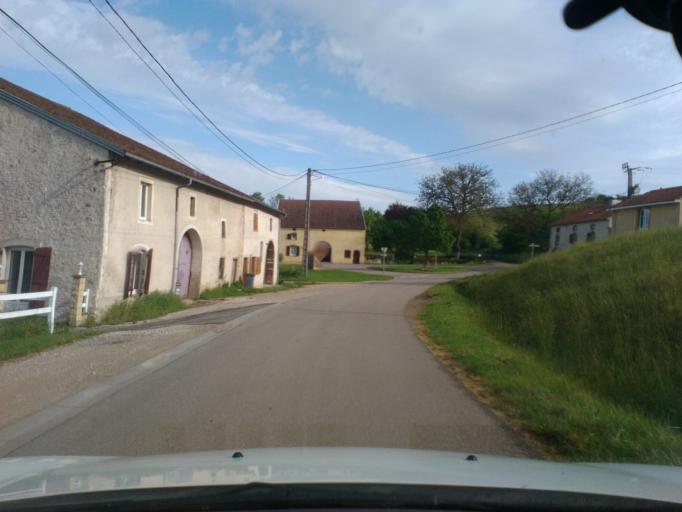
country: FR
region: Lorraine
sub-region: Departement des Vosges
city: Mirecourt
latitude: 48.3321
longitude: 6.1506
